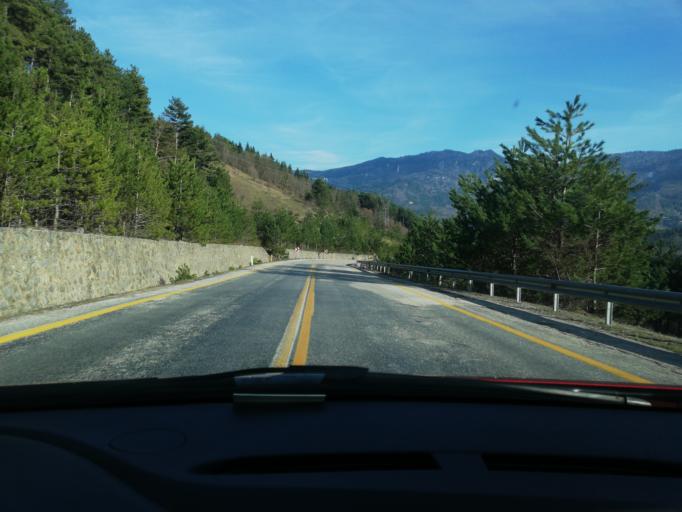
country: TR
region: Kastamonu
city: Senpazar
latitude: 41.7849
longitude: 33.1630
